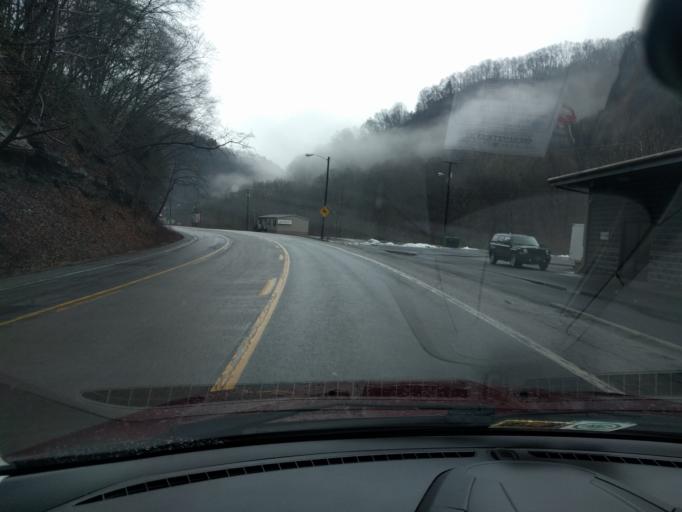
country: US
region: West Virginia
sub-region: McDowell County
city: Welch
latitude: 37.4326
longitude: -81.5648
